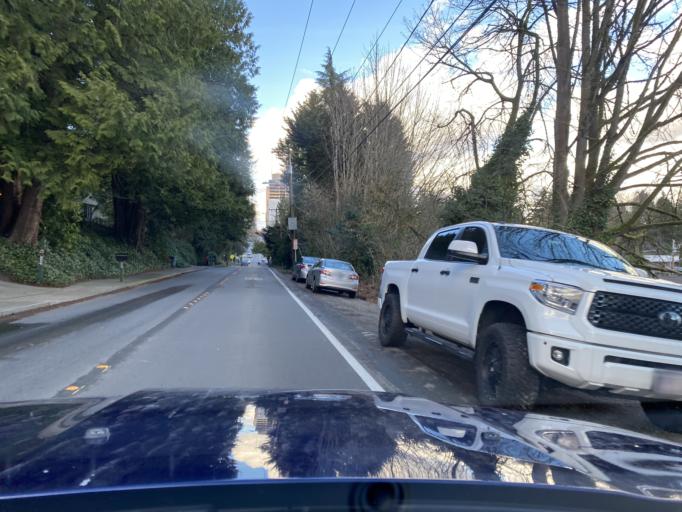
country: US
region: Washington
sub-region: King County
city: Bellevue
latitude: 47.6065
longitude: -122.1960
